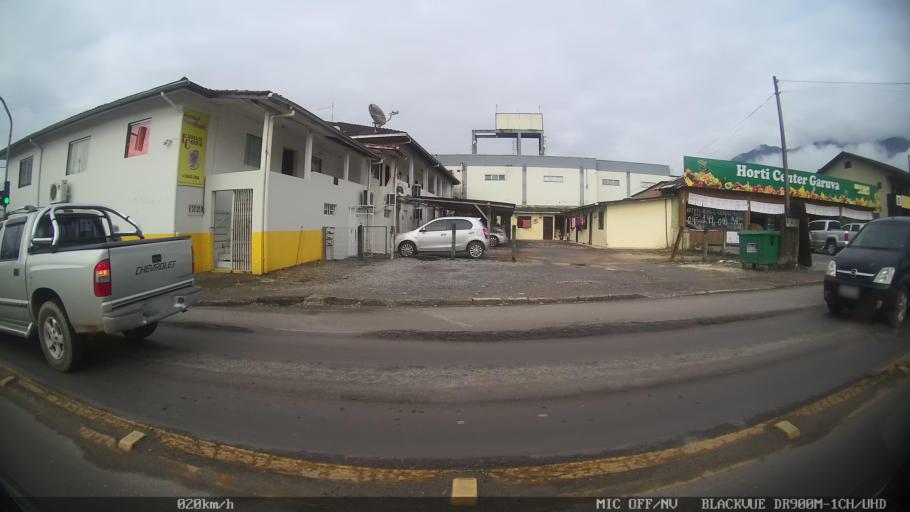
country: BR
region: Santa Catarina
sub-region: Joinville
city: Joinville
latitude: -26.0298
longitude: -48.8557
